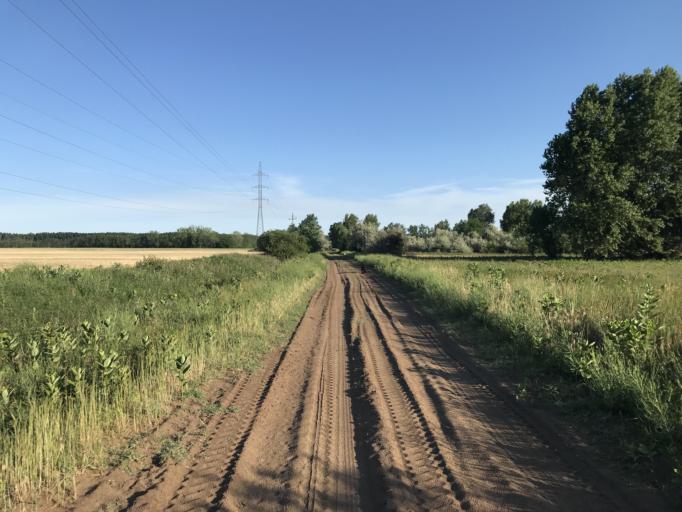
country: HU
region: Bacs-Kiskun
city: Tiszakecske
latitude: 46.9717
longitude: 20.0635
